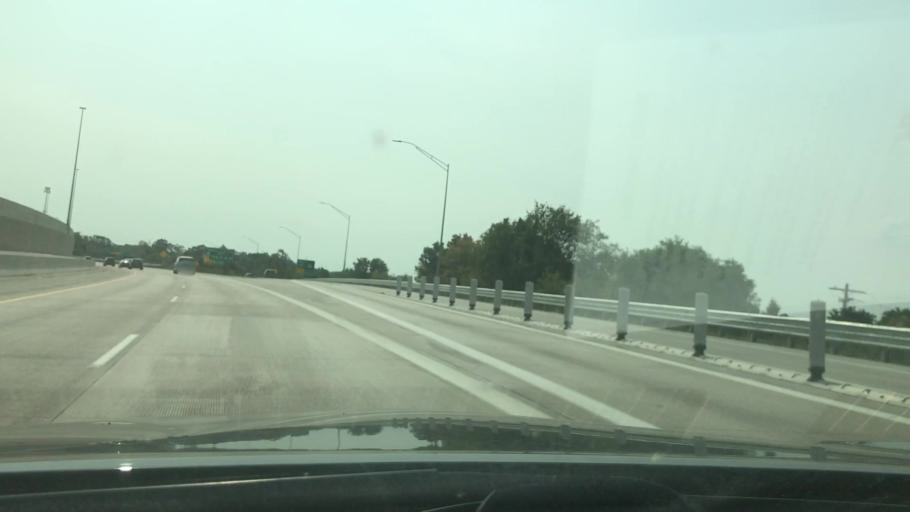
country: US
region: Michigan
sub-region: Livingston County
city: Brighton
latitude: 42.5277
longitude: -83.7629
